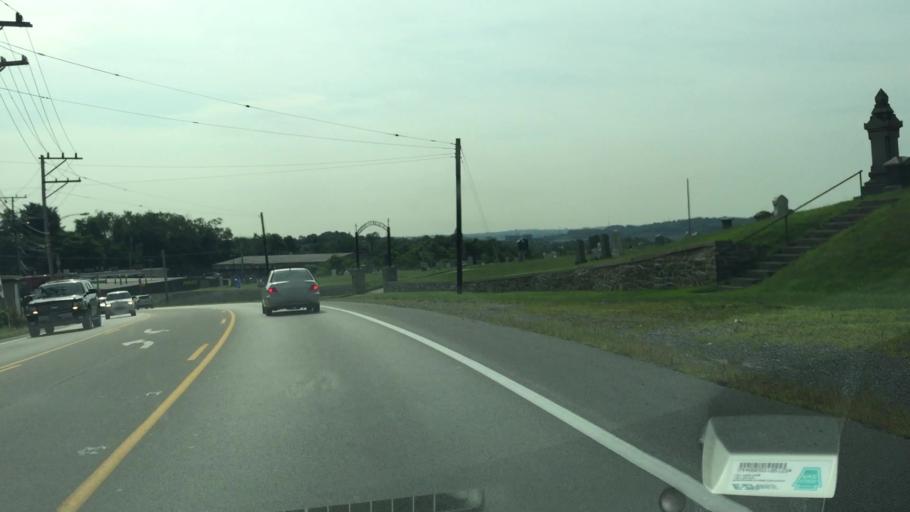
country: US
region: Pennsylvania
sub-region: Allegheny County
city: Rennerdale
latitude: 40.4443
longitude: -80.1489
